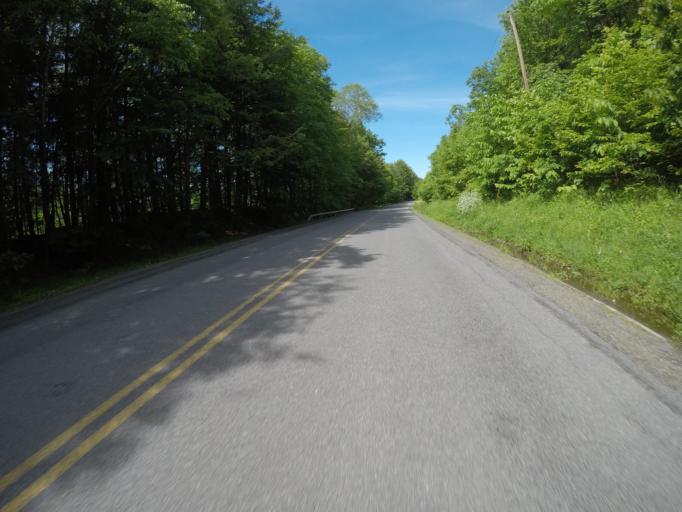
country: US
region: New York
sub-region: Delaware County
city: Delhi
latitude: 42.1026
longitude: -74.8258
